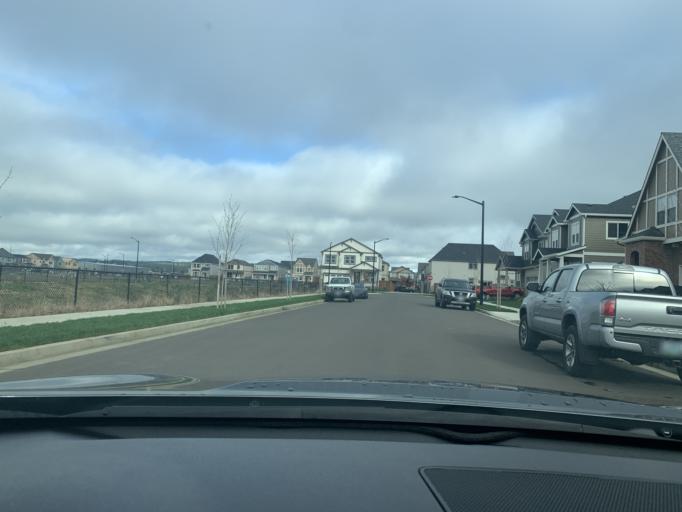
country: US
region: Oregon
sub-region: Washington County
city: North Plains
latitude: 45.5928
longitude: -122.9753
